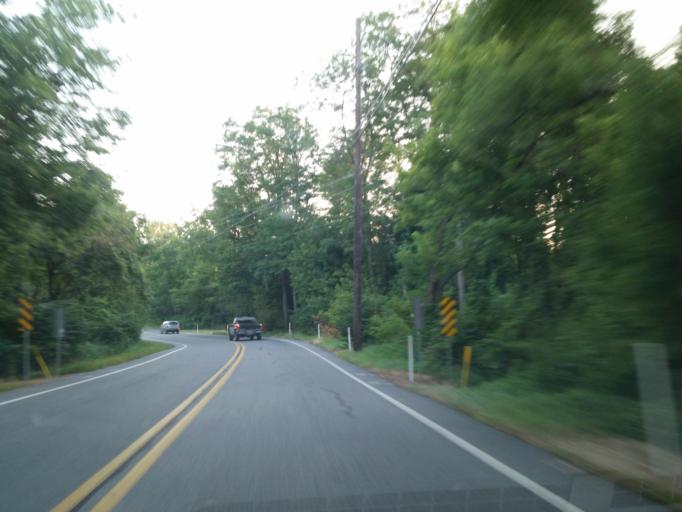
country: US
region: Pennsylvania
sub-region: Lebanon County
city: Cornwall
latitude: 40.2800
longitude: -76.4081
